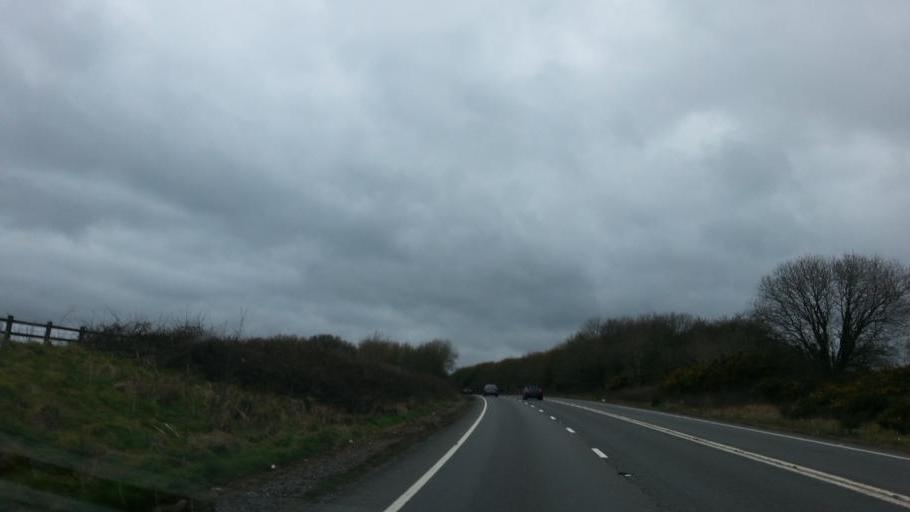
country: GB
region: England
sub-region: Devon
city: Tiverton
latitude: 50.9369
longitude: -3.5488
